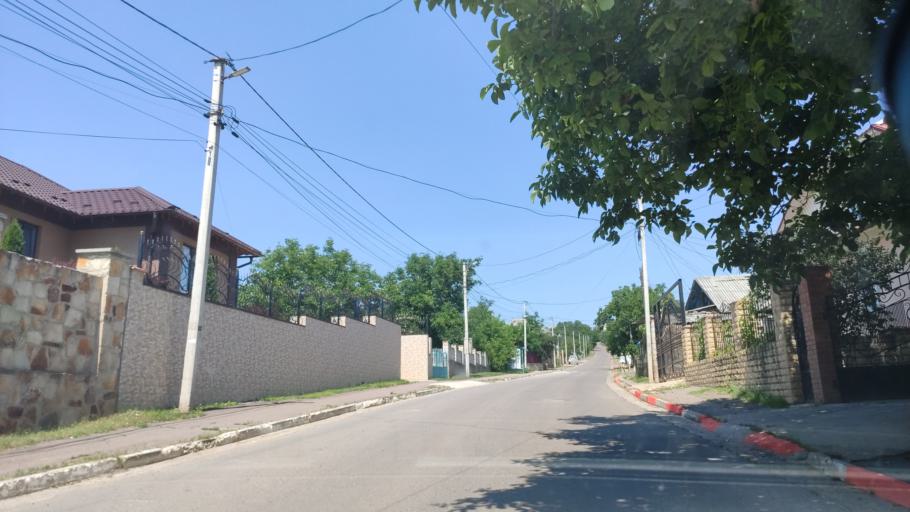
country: MD
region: Raionul Soroca
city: Soroca
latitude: 48.1690
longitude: 28.2999
